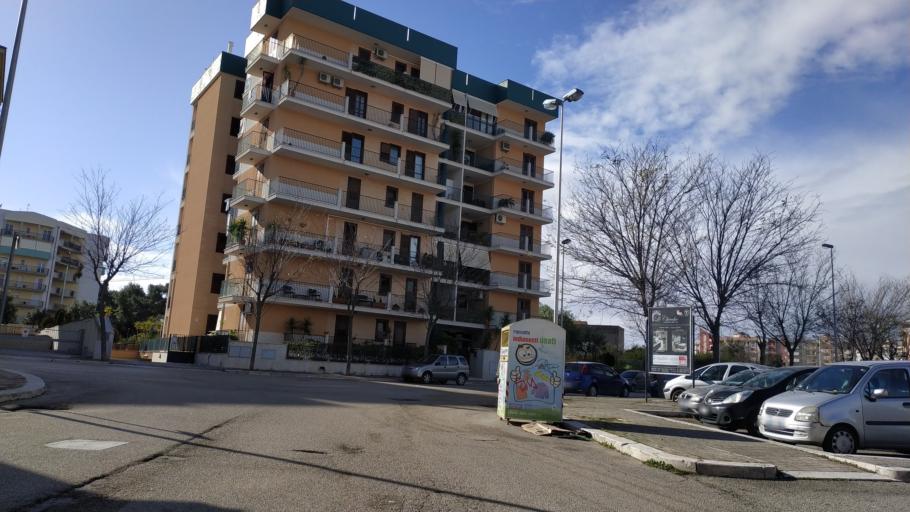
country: IT
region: Apulia
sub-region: Provincia di Barletta - Andria - Trani
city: Andria
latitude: 41.2361
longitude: 16.3053
